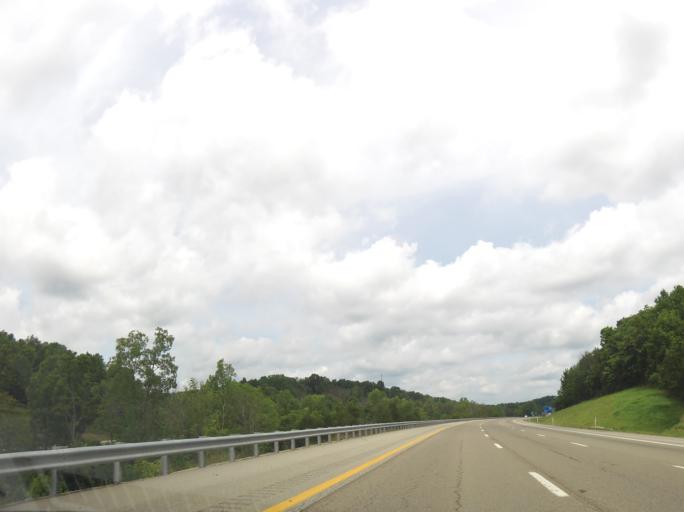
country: US
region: Kentucky
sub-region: Grant County
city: Williamstown
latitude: 38.4712
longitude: -84.5792
